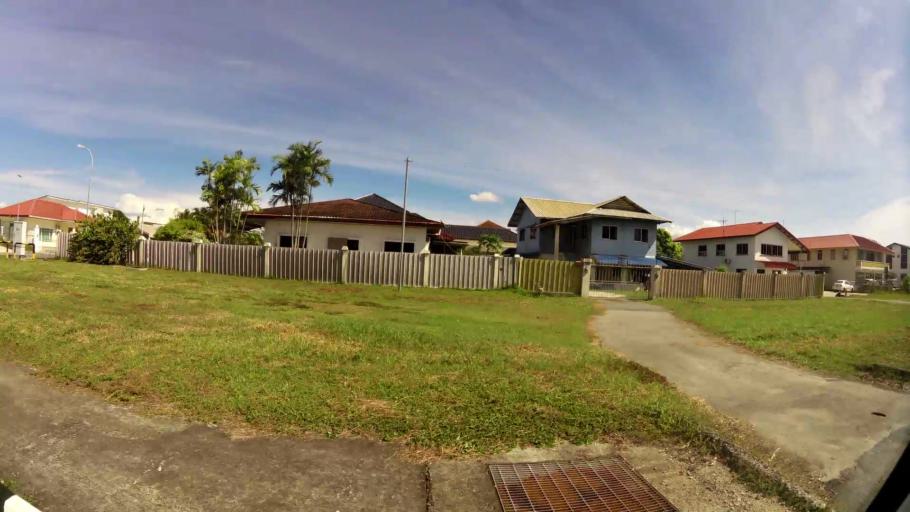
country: BN
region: Belait
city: Kuala Belait
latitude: 4.5890
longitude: 114.2064
